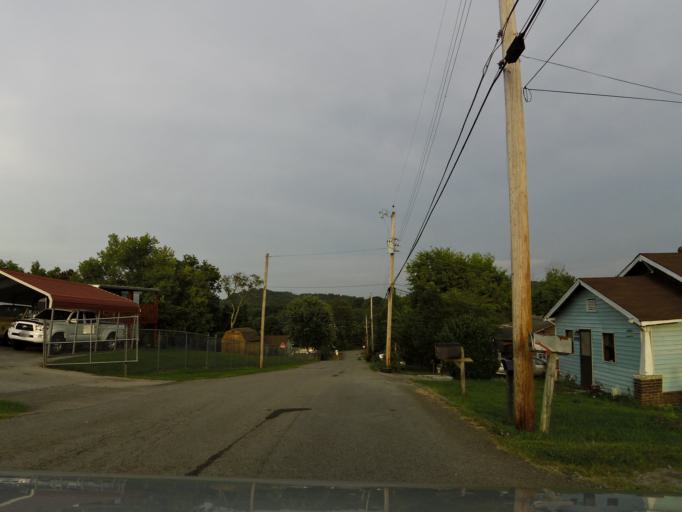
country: US
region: Tennessee
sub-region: Knox County
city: Knoxville
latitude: 35.9306
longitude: -83.9246
